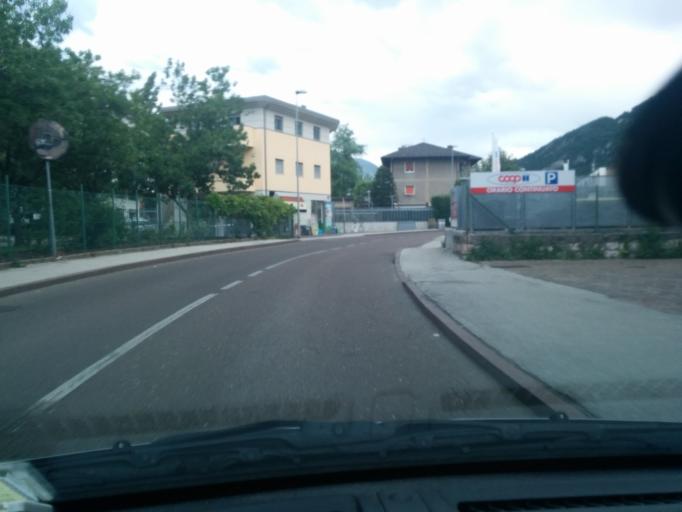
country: IT
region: Trentino-Alto Adige
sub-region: Provincia di Trento
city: Trento
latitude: 46.0864
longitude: 11.1216
